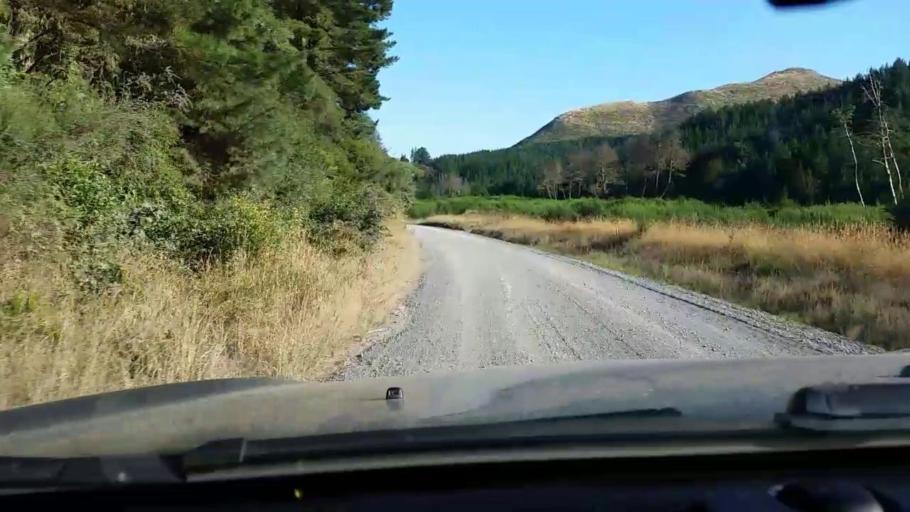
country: NZ
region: Waikato
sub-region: Taupo District
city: Taupo
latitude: -38.4650
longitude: 176.1617
